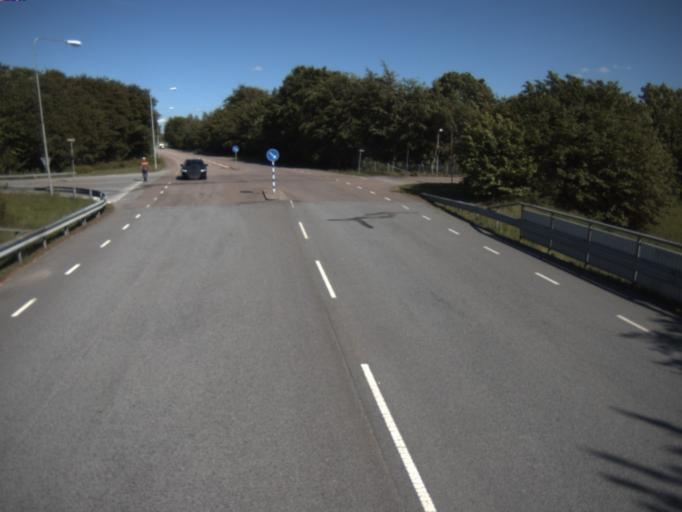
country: SE
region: Skane
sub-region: Helsingborg
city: Rydeback
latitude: 55.9656
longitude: 12.7716
